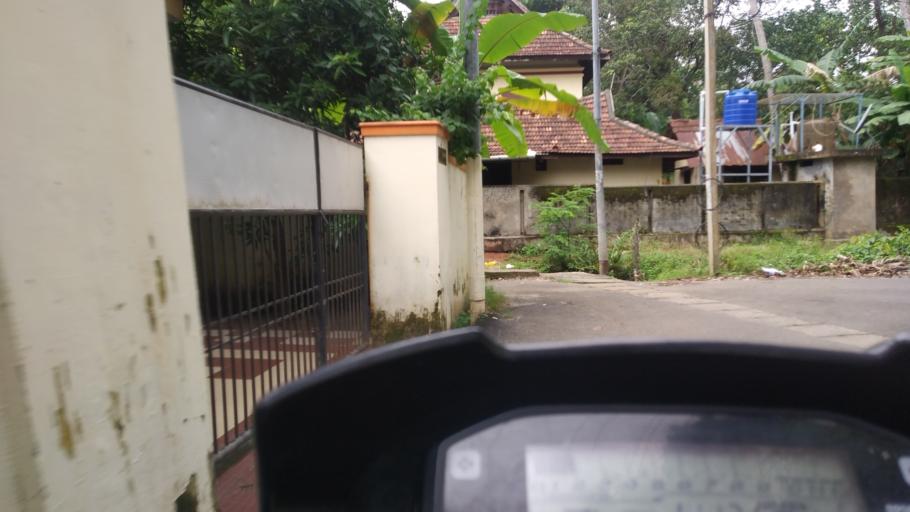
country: IN
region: Kerala
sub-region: Ernakulam
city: Elur
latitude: 10.0586
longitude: 76.2182
